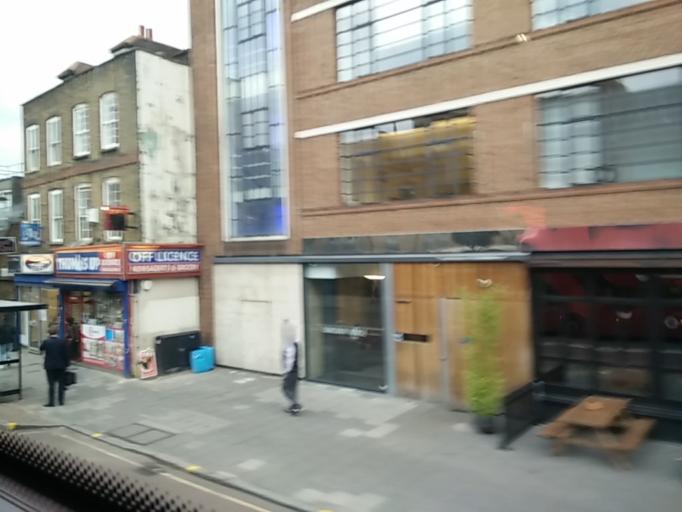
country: GB
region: England
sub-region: Greater London
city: Islington
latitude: 51.5367
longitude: -0.1013
